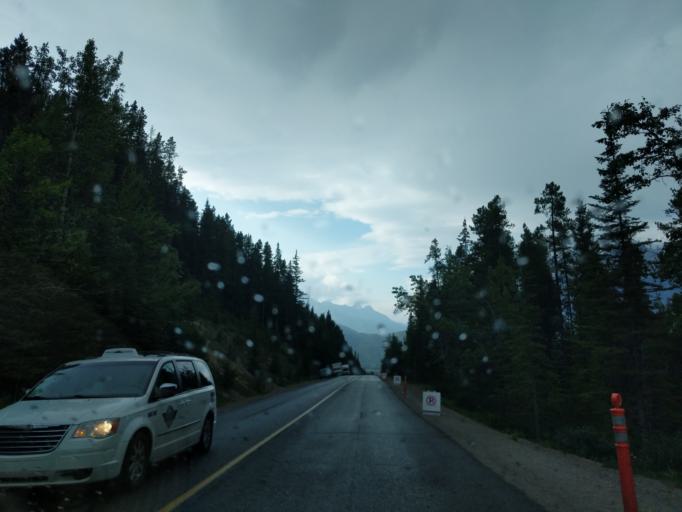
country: CA
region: Alberta
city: Banff
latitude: 51.1534
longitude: -115.5616
